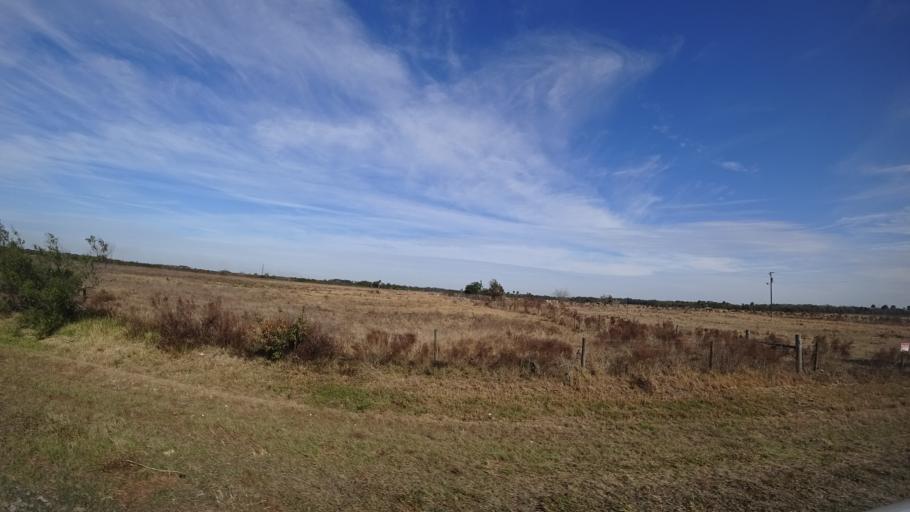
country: US
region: Florida
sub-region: Manatee County
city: Ellenton
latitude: 27.6012
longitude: -82.4750
